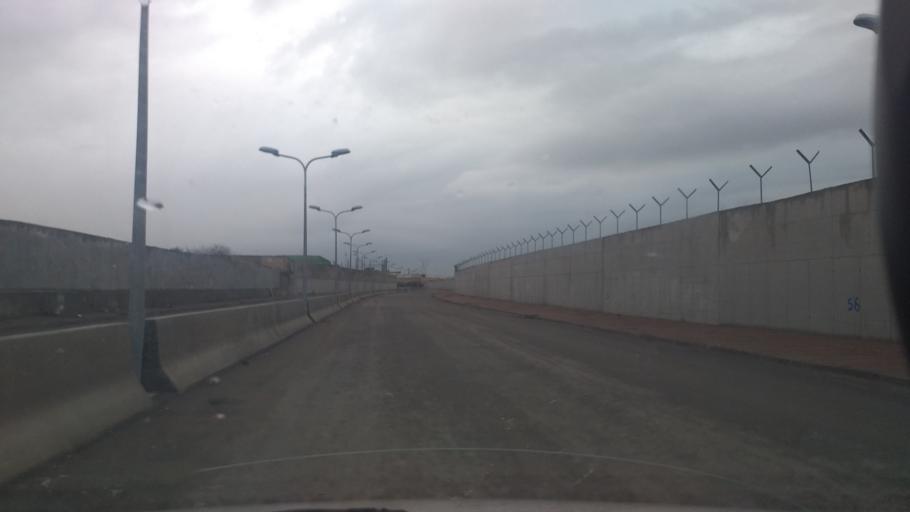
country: TN
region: Ariana
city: Ariana
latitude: 36.8556
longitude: 10.2131
